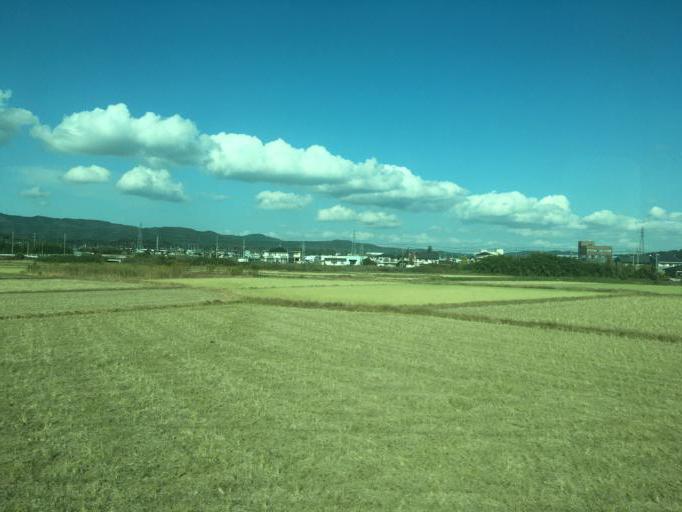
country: JP
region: Ibaraki
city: Kasama
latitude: 36.3747
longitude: 140.2409
